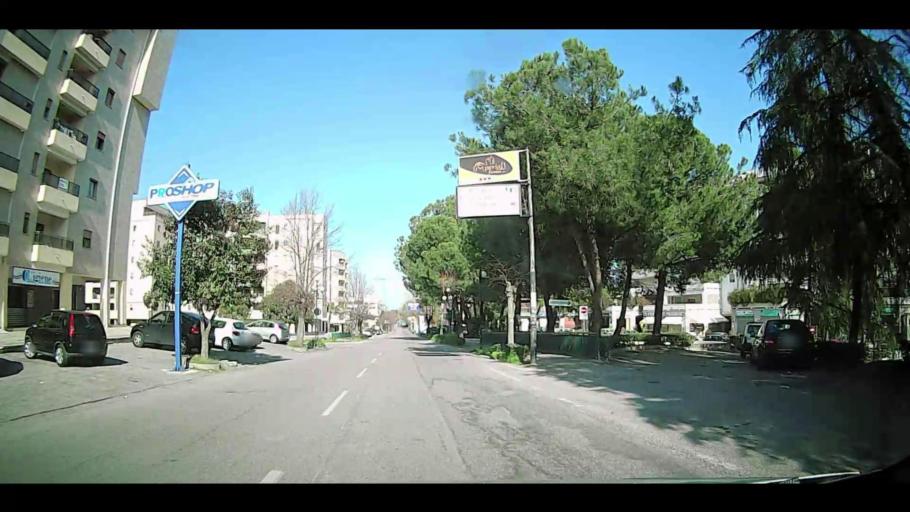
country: IT
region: Calabria
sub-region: Provincia di Cosenza
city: Quattromiglia
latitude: 39.3430
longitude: 16.2439
